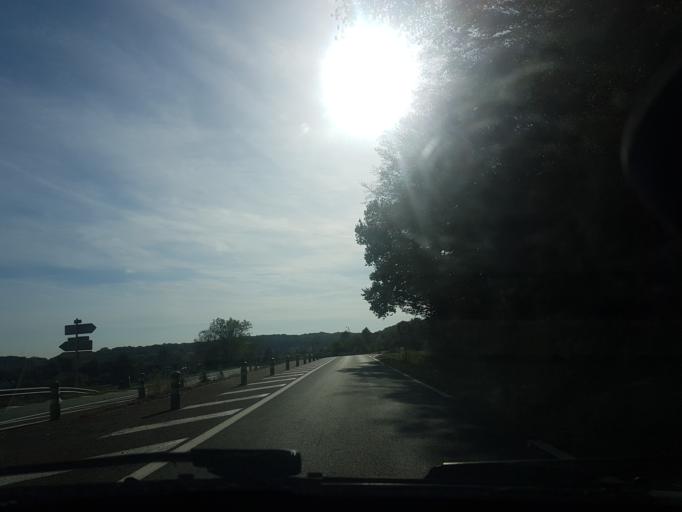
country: FR
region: Franche-Comte
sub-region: Territoire de Belfort
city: Offemont
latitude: 47.6593
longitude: 6.9035
